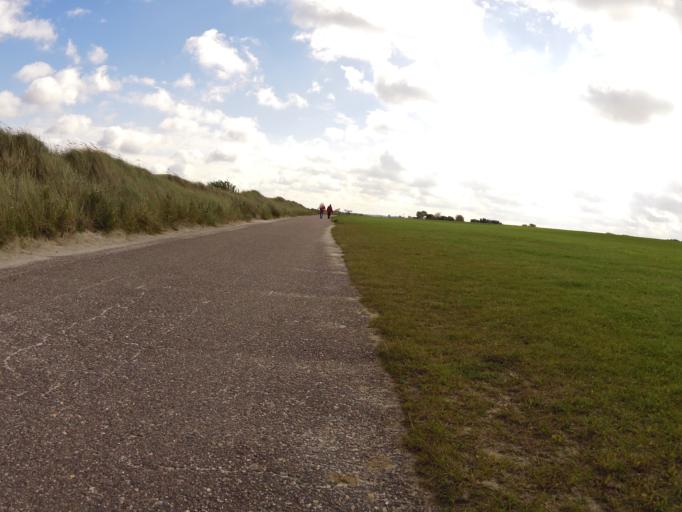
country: DE
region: Schleswig-Holstein
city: Krummbek
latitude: 54.4229
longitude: 10.3967
